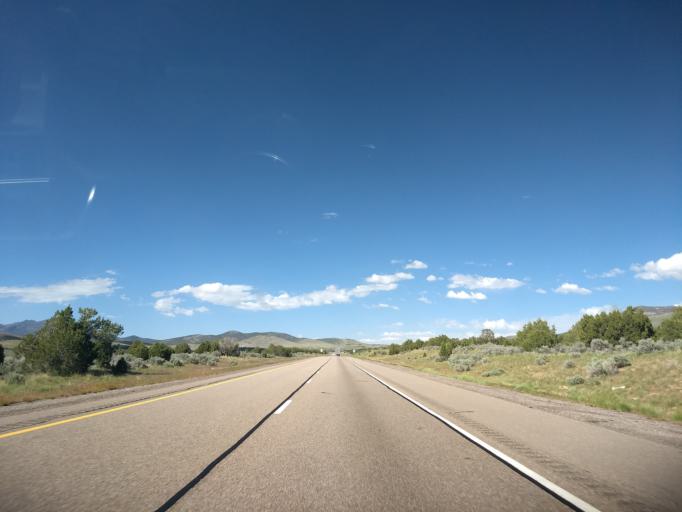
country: US
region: Utah
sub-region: Millard County
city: Fillmore
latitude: 39.1578
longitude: -112.2253
